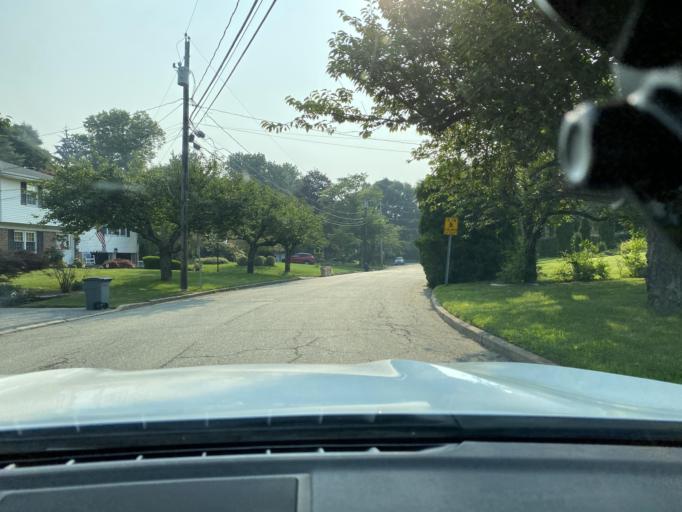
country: US
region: New Jersey
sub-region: Bergen County
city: Mahwah
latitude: 41.0932
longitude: -74.1315
